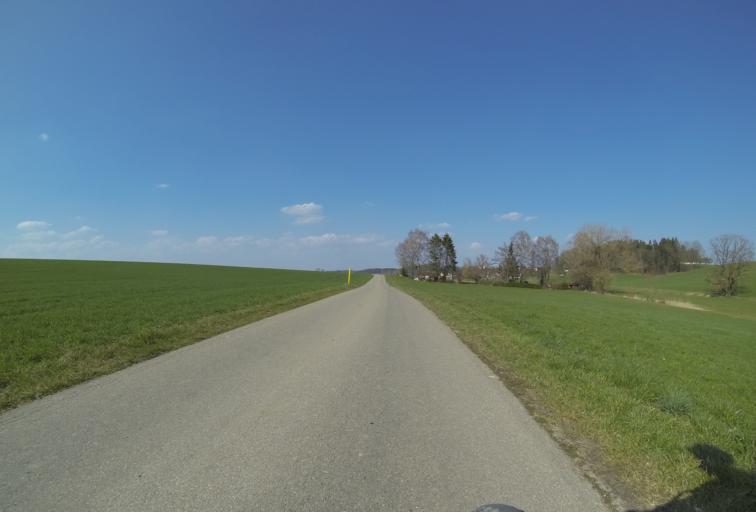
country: DE
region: Baden-Wuerttemberg
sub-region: Tuebingen Region
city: Huttisheim
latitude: 48.2542
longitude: 9.9516
